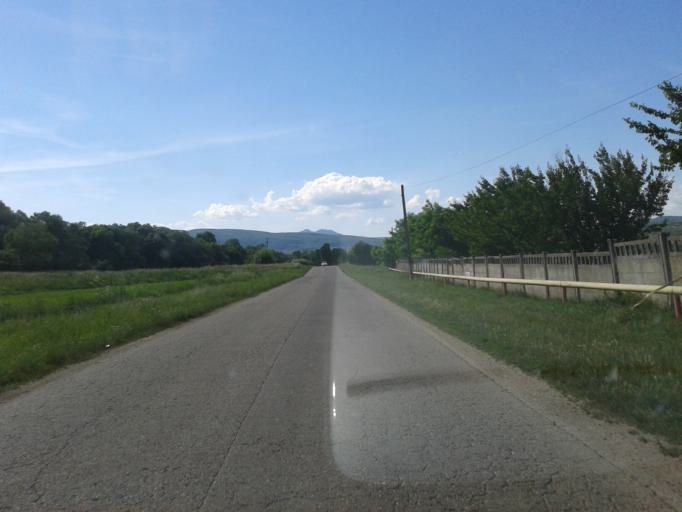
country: RO
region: Hunedoara
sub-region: Comuna Geoagiu
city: Geoagiu
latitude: 45.8894
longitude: 23.2352
